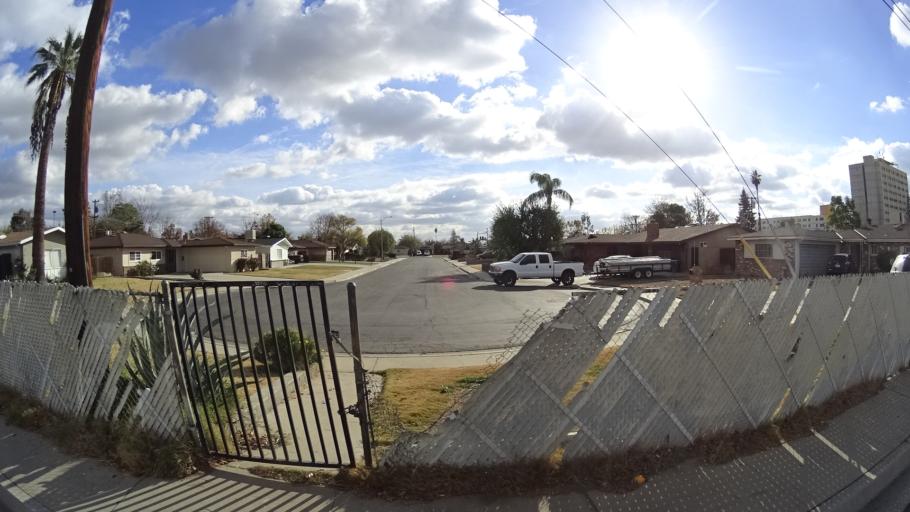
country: US
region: California
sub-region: Kern County
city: Bakersfield
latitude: 35.3321
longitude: -119.0343
